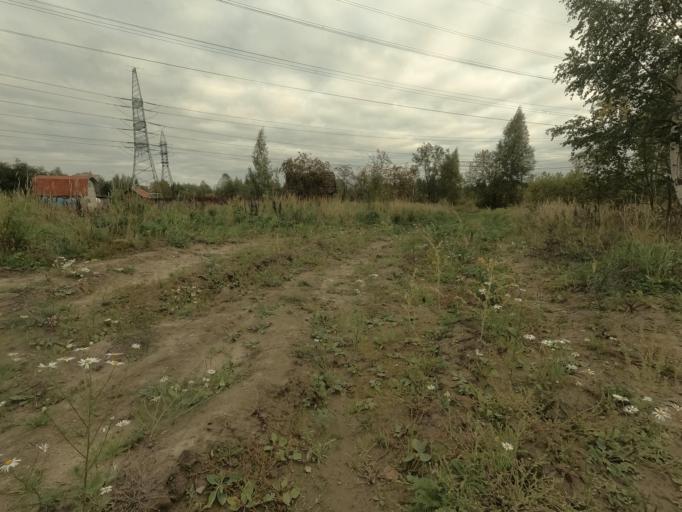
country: RU
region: St.-Petersburg
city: Metallostroy
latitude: 59.8147
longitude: 30.5468
